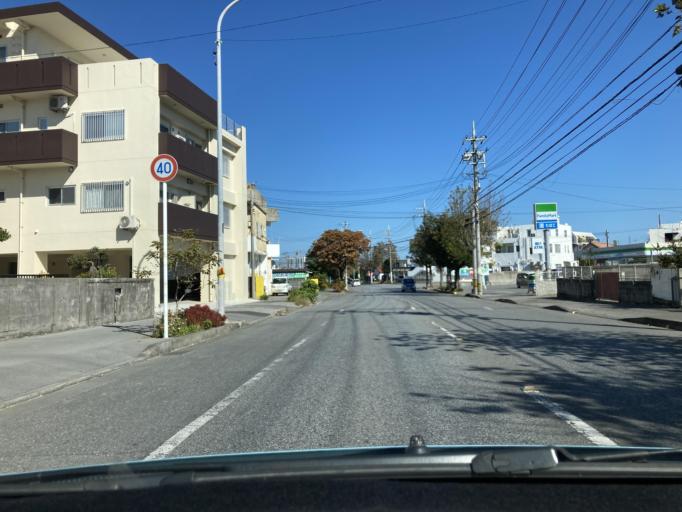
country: JP
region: Okinawa
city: Gushikawa
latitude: 26.3677
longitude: 127.8587
